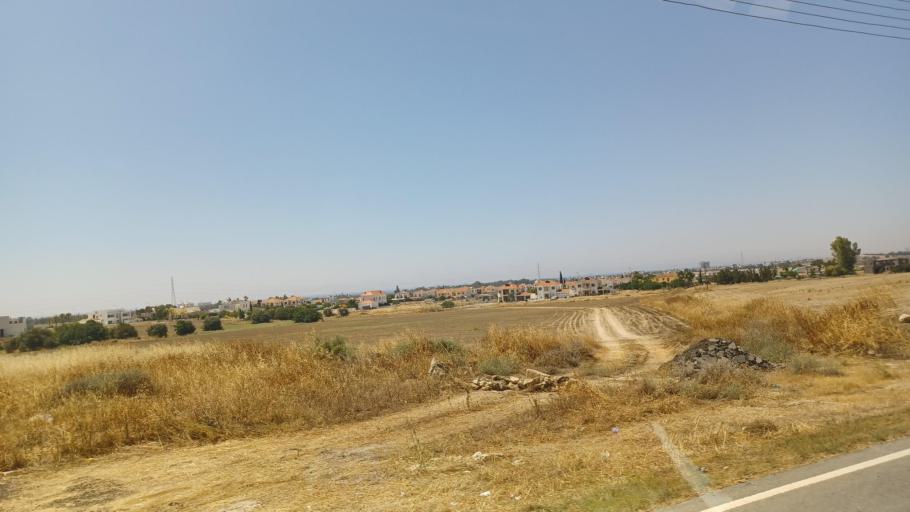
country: CY
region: Larnaka
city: Pyla
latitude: 34.9965
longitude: 33.6803
